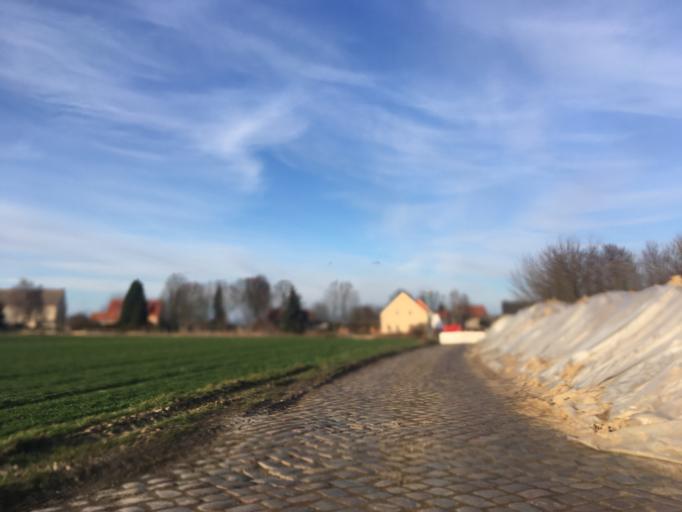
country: DE
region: Berlin
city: Blankenfelde
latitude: 52.6153
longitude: 13.3853
